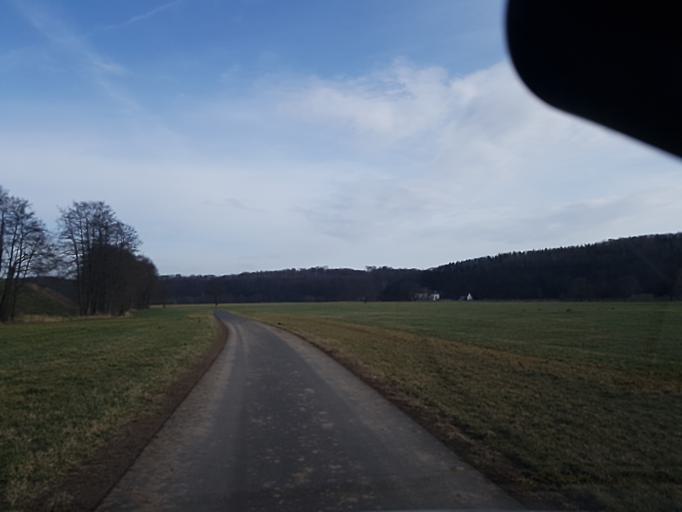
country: DE
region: Saxony
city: Grossweitzschen
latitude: 51.1469
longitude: 13.0074
